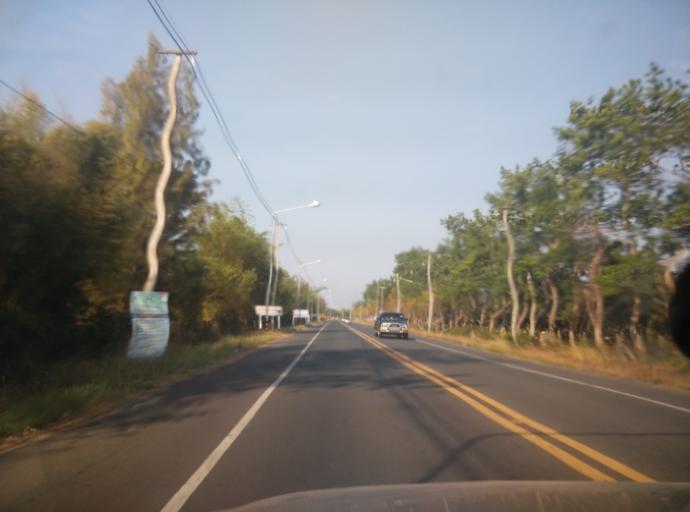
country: TH
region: Sisaket
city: Si Sa Ket
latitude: 15.1122
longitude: 104.2738
